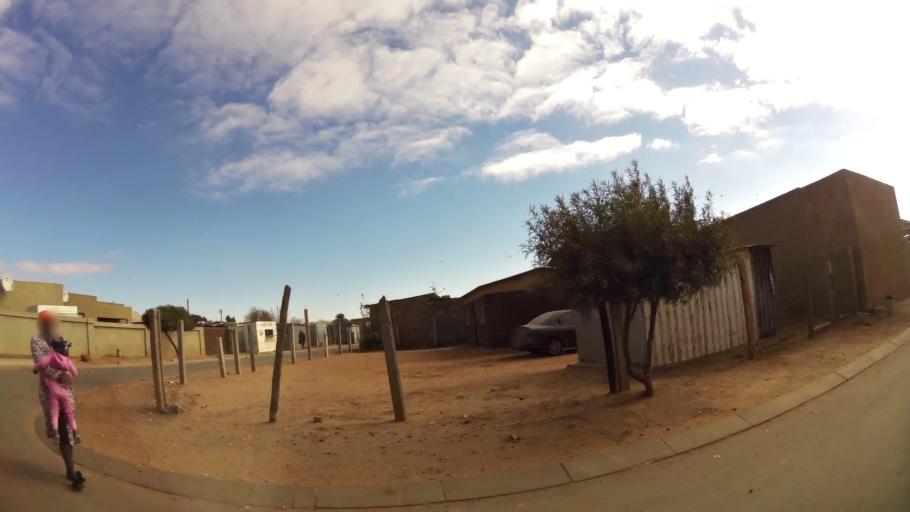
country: ZA
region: Gauteng
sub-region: City of Johannesburg Metropolitan Municipality
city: Modderfontein
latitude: -26.0507
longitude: 28.1775
